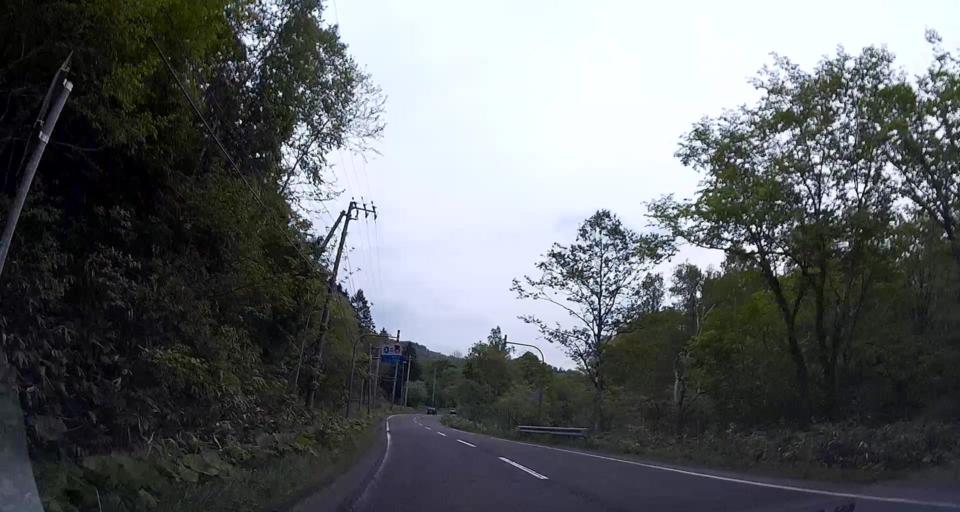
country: JP
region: Hokkaido
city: Shiraoi
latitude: 42.6903
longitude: 141.1052
